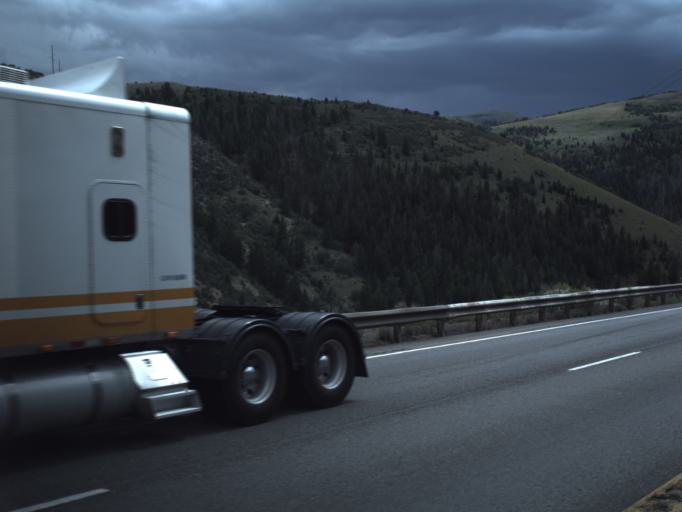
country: US
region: Utah
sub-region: Carbon County
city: Helper
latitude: 39.8131
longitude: -110.9397
